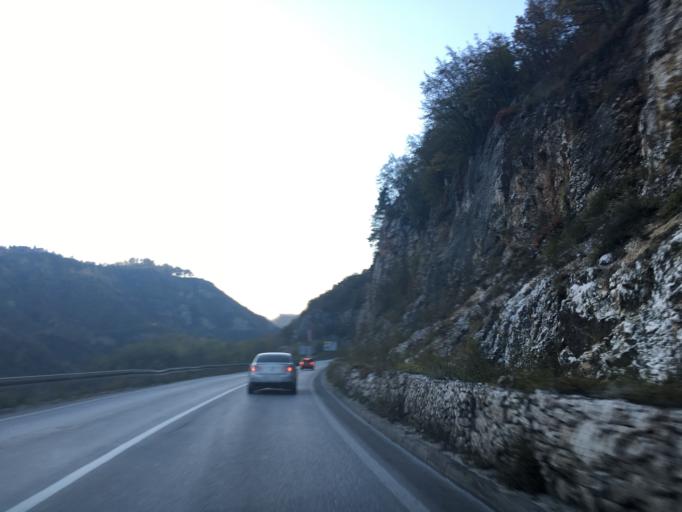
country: BA
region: Federation of Bosnia and Herzegovina
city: Kobilja Glava
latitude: 43.8468
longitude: 18.4698
